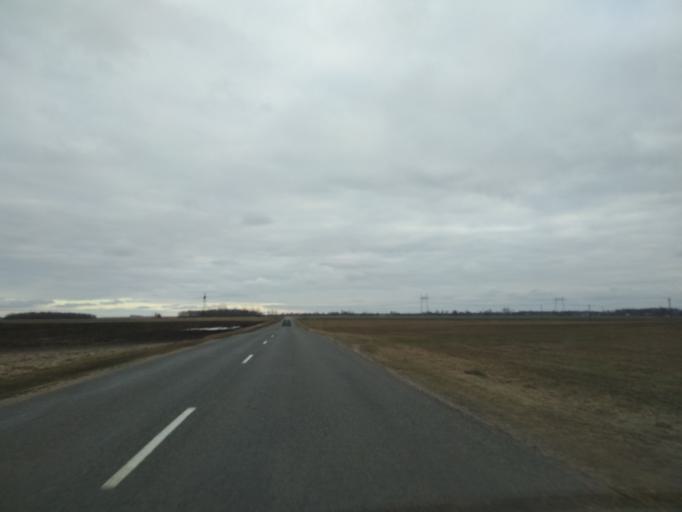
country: BY
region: Minsk
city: Mar''ina Horka
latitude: 53.5612
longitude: 28.0444
